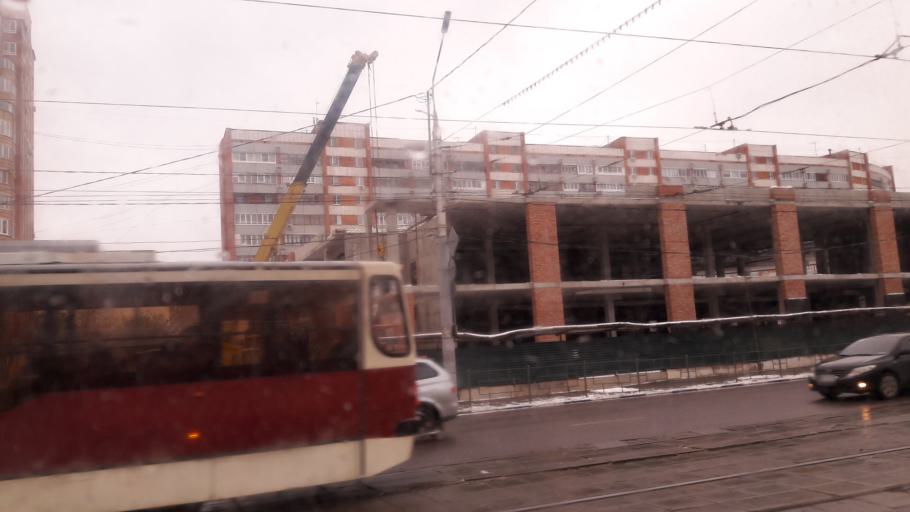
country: RU
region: Tula
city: Tula
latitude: 54.1945
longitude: 37.6123
